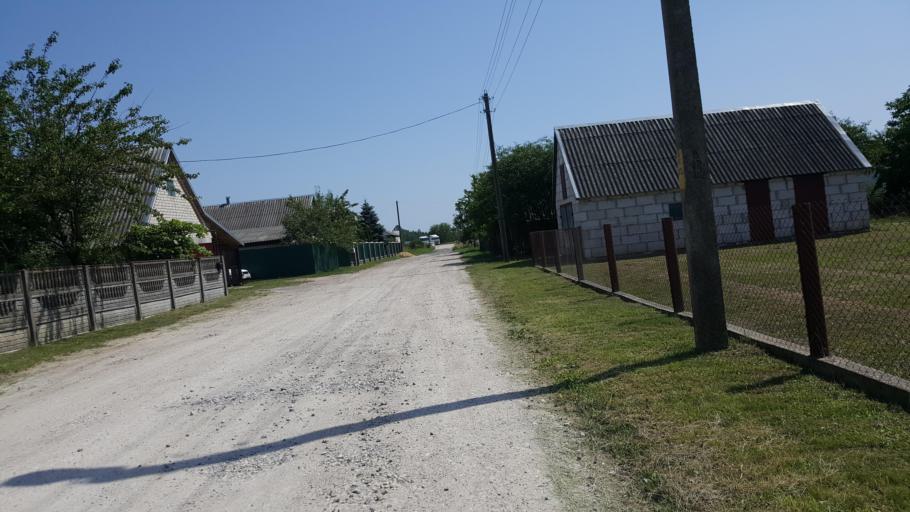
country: BY
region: Brest
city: Zhabinka
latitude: 52.1866
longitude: 23.9975
